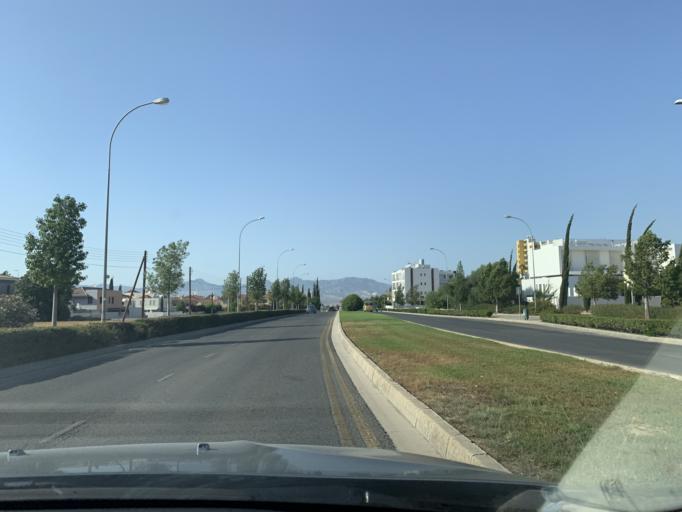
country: CY
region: Lefkosia
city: Nicosia
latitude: 35.1506
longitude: 33.3815
